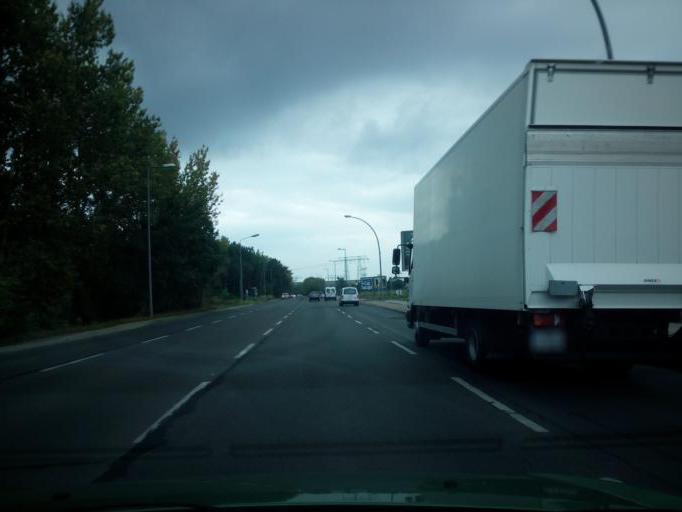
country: DE
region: Berlin
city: Rummelsburg
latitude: 52.4814
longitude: 13.5024
